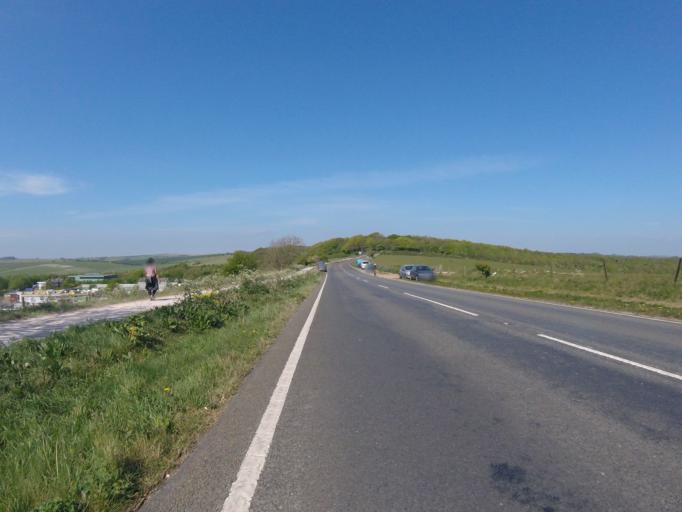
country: GB
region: England
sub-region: Brighton and Hove
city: Brighton
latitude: 50.8658
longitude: -0.1200
